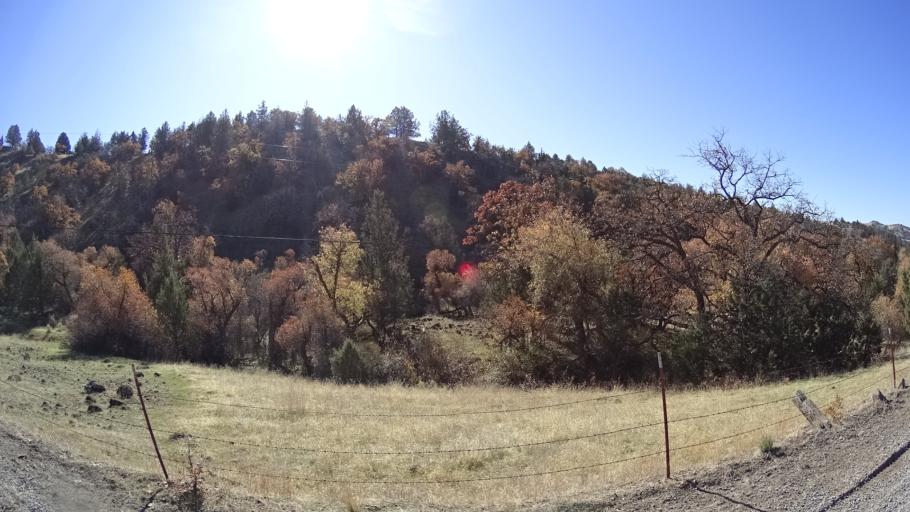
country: US
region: California
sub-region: Siskiyou County
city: Montague
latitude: 41.7935
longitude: -122.3443
